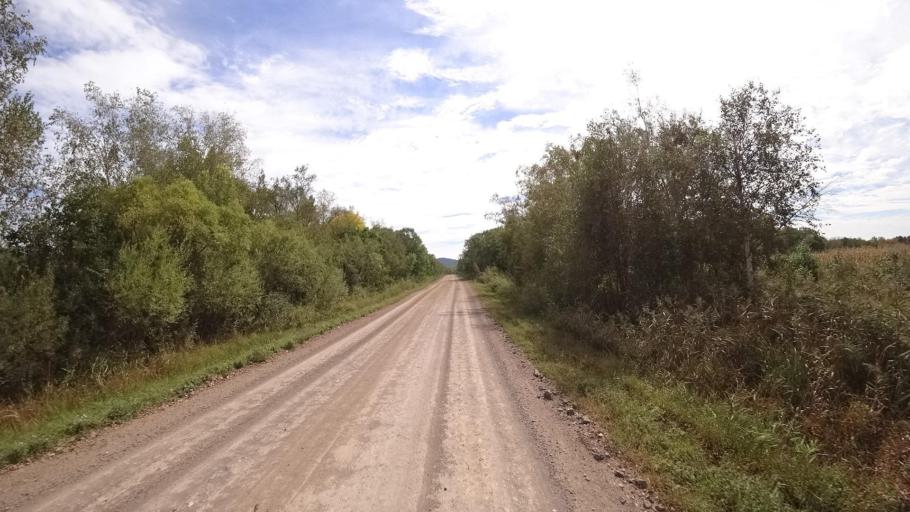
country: RU
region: Primorskiy
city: Yakovlevka
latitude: 44.6022
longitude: 133.6039
